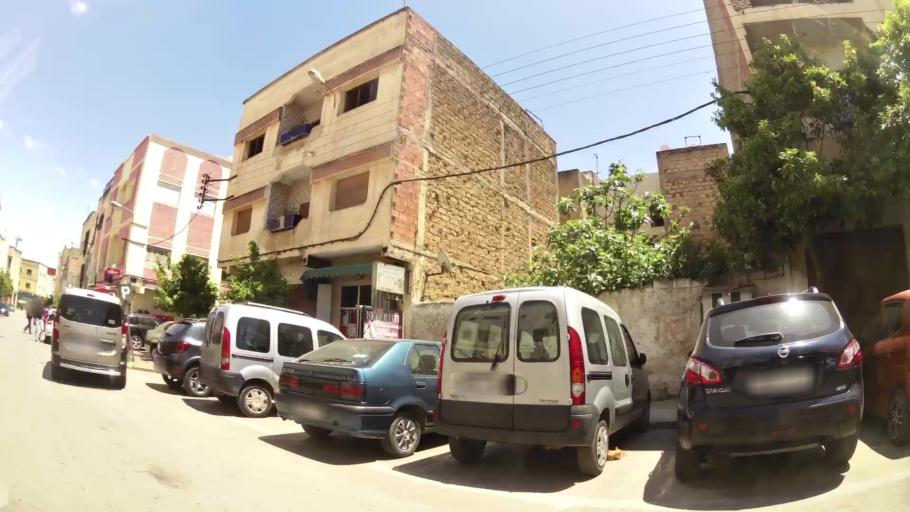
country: MA
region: Fes-Boulemane
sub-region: Fes
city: Fes
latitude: 34.0149
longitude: -4.9893
